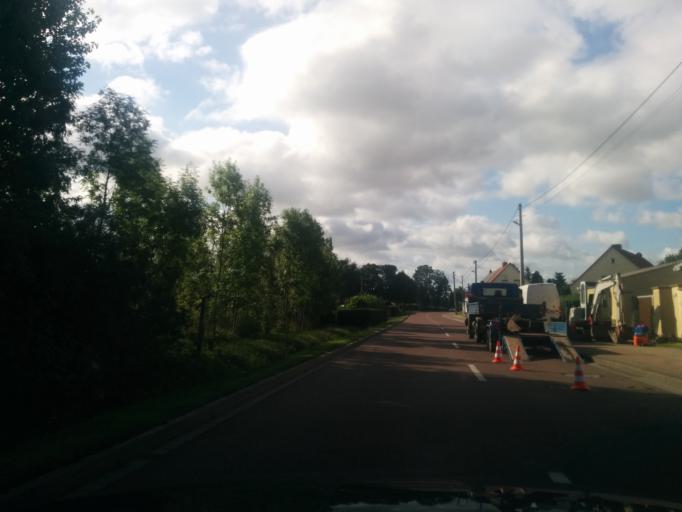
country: DE
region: Saxony-Anhalt
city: Bennstedt
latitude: 51.4621
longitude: 11.8214
